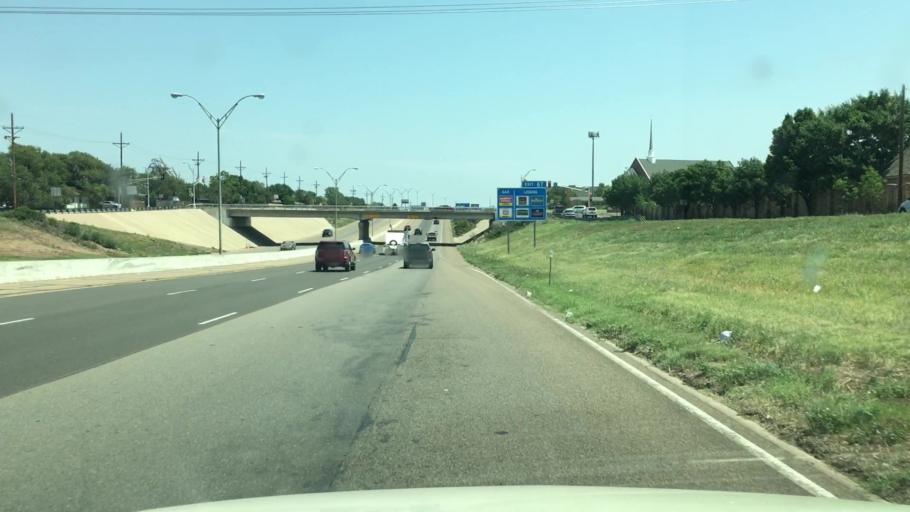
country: US
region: Texas
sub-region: Potter County
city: Amarillo
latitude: 35.1909
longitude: -101.8952
